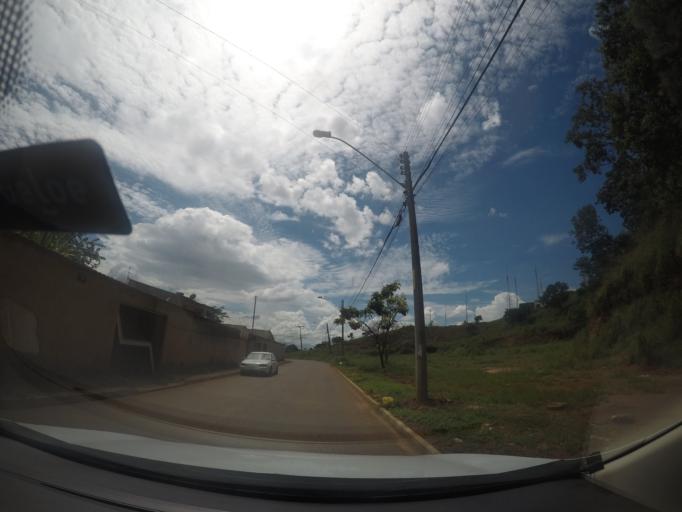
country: BR
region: Goias
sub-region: Goiania
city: Goiania
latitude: -16.6612
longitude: -49.3444
